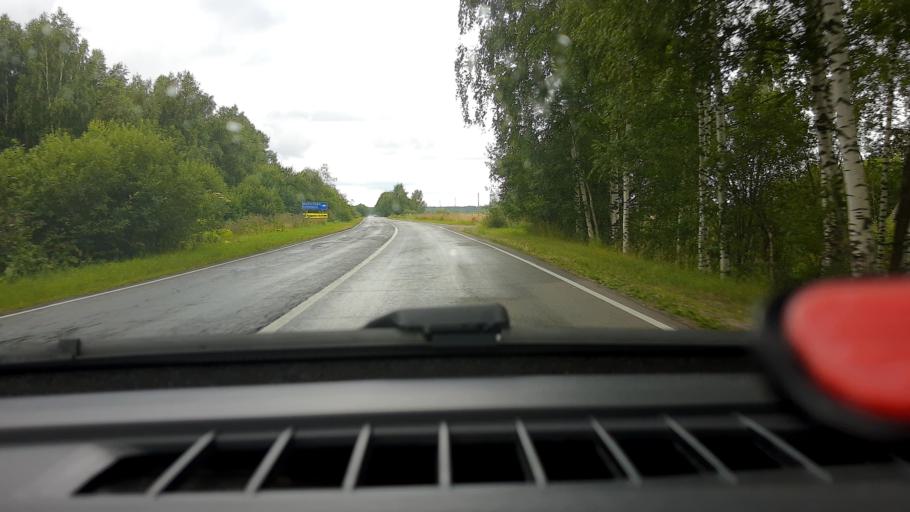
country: RU
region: Nizjnij Novgorod
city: Neklyudovo
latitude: 56.5239
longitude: 43.8679
